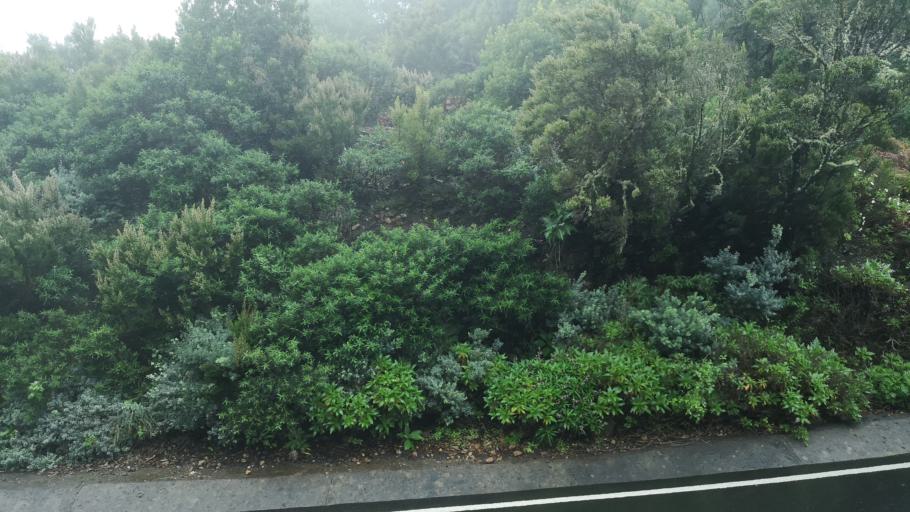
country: ES
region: Canary Islands
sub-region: Provincia de Santa Cruz de Tenerife
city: Alajero
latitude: 28.1097
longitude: -17.2136
